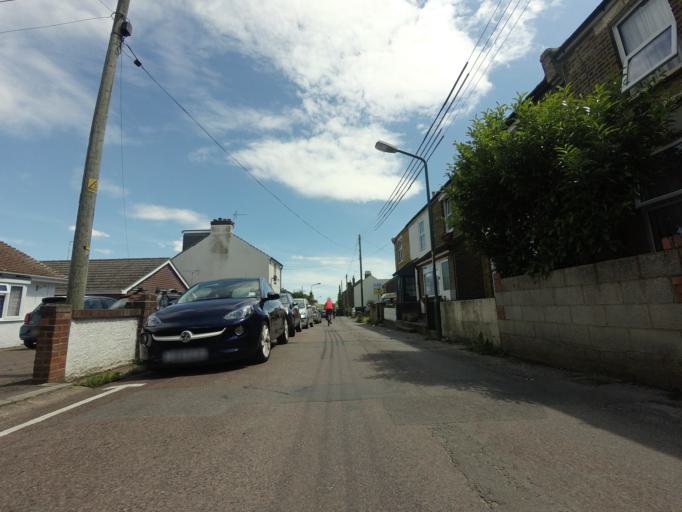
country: GB
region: England
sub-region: Kent
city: Cliffe
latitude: 51.4621
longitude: 0.5008
